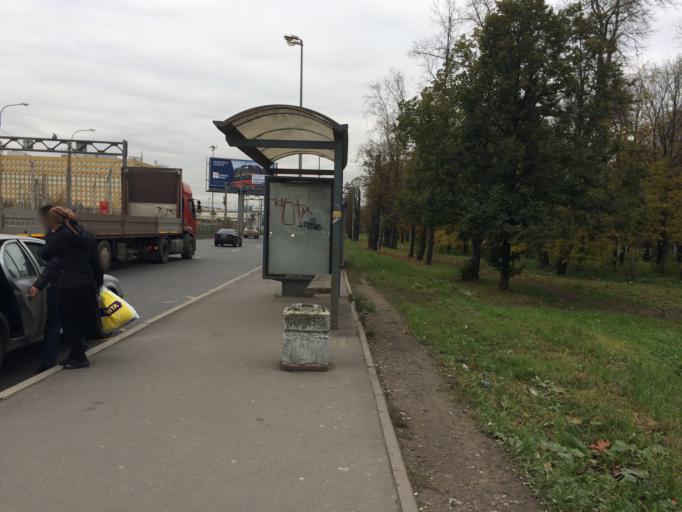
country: RU
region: Leningrad
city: Rybatskoye
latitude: 59.8478
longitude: 30.4833
